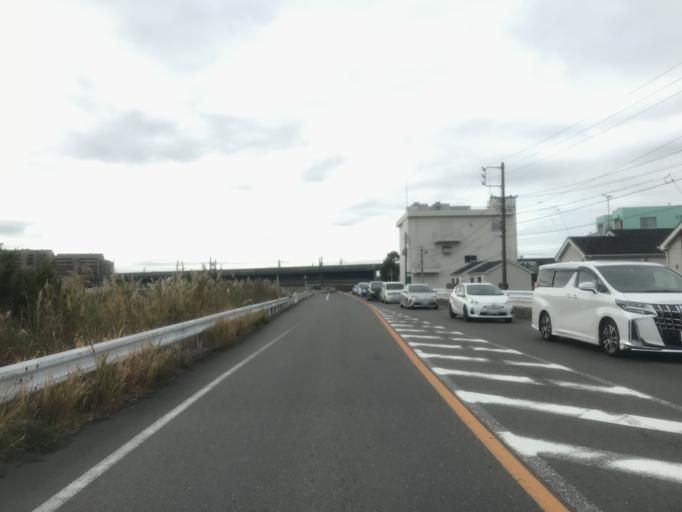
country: JP
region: Aichi
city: Nagoya-shi
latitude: 35.2051
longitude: 136.8572
